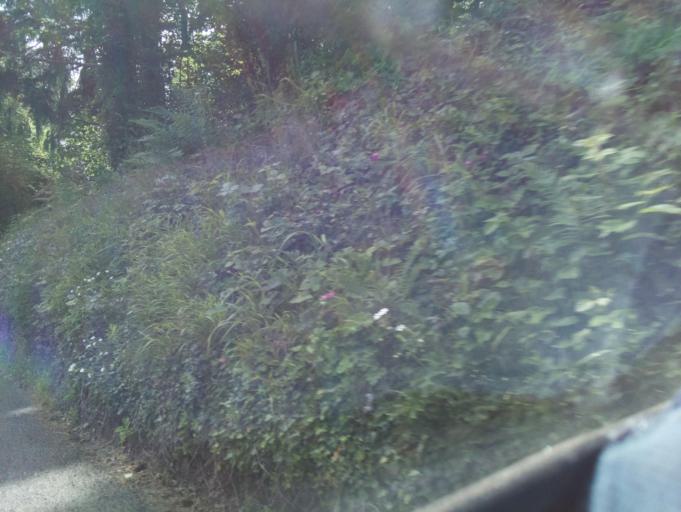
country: GB
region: England
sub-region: Herefordshire
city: Llanrothal
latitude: 51.8819
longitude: -2.7765
